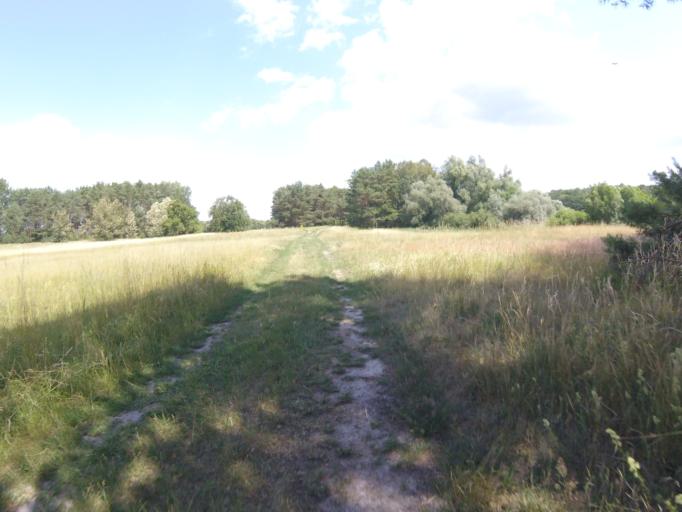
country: DE
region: Brandenburg
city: Bestensee
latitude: 52.2189
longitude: 13.6451
